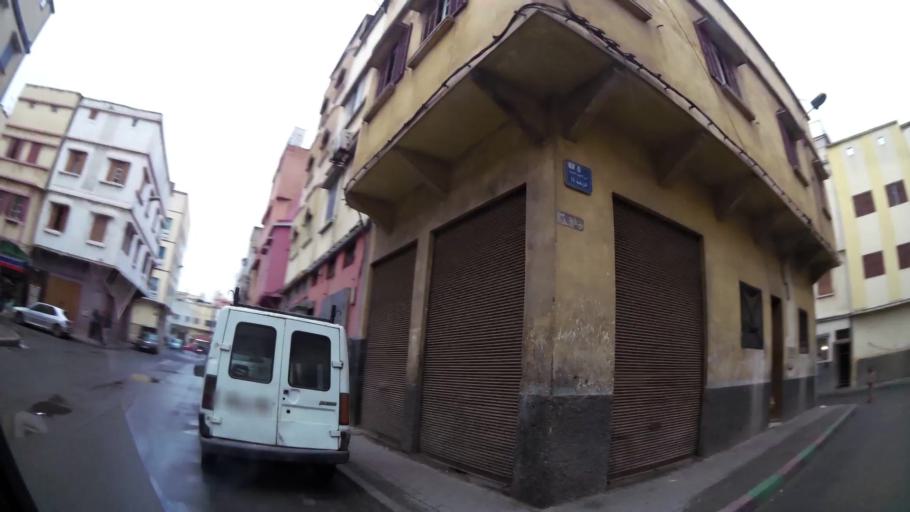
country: MA
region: Grand Casablanca
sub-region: Casablanca
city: Casablanca
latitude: 33.5525
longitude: -7.5810
